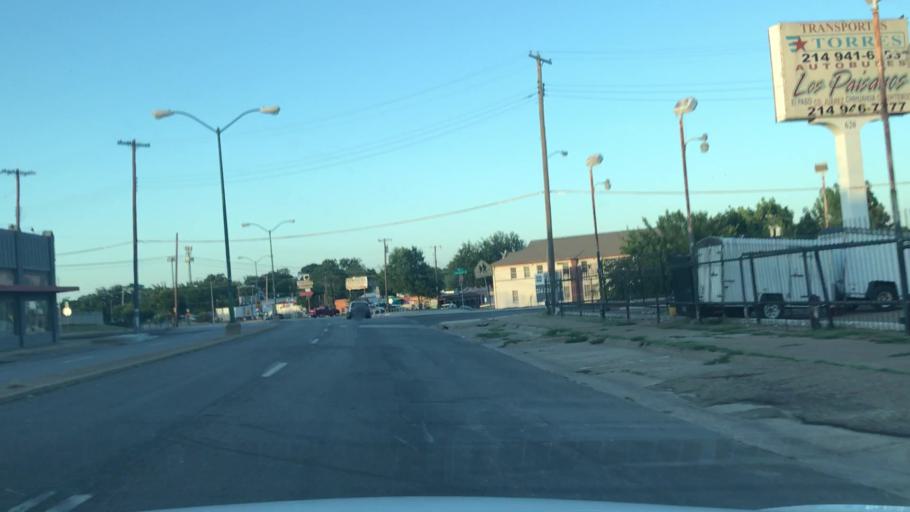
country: US
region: Texas
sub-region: Dallas County
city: Dallas
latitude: 32.7477
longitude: -96.8146
